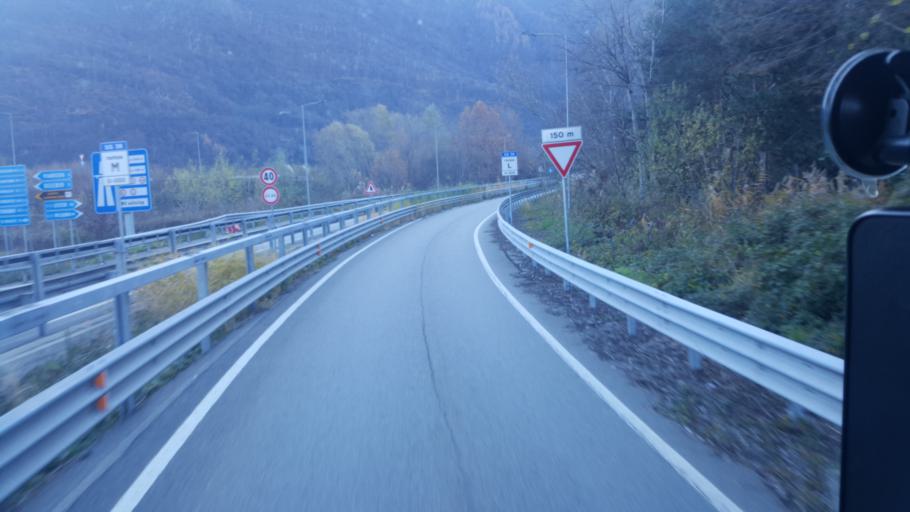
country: IT
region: Lombardy
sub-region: Provincia di Sondrio
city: Piantedo
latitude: 46.1424
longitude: 9.4101
